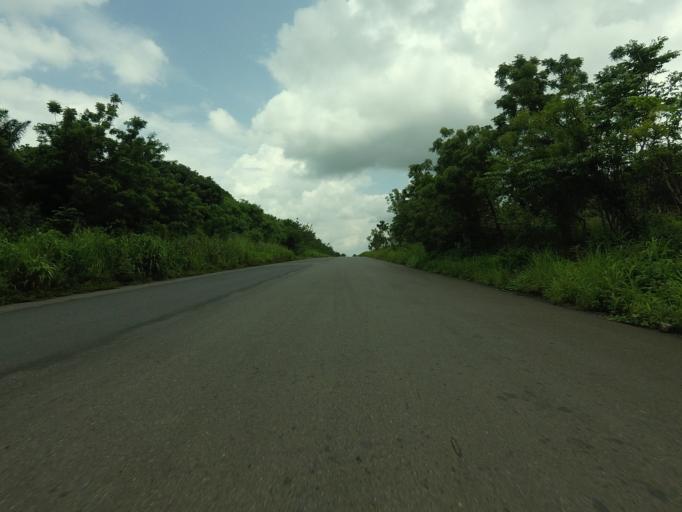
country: GH
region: Volta
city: Ho
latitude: 6.6104
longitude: 0.2997
